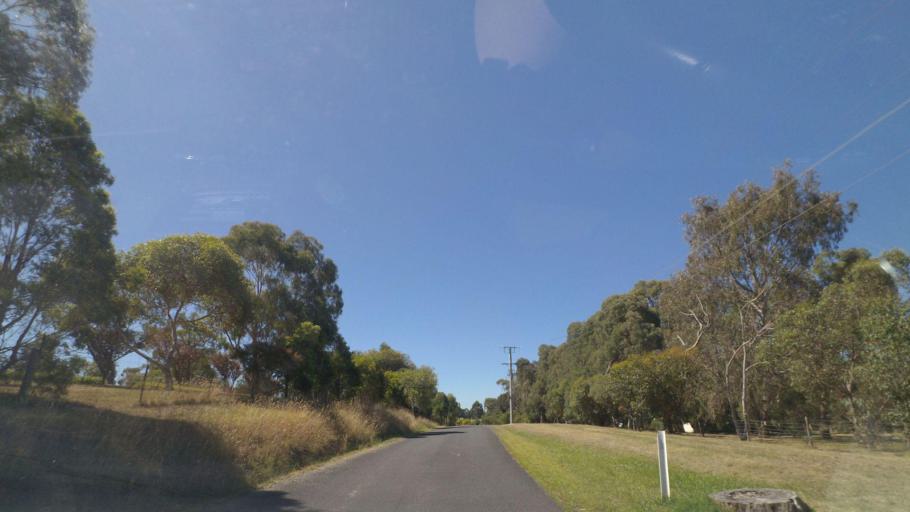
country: AU
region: Victoria
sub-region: Yarra Ranges
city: Chirnside Park
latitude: -37.7401
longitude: 145.3286
